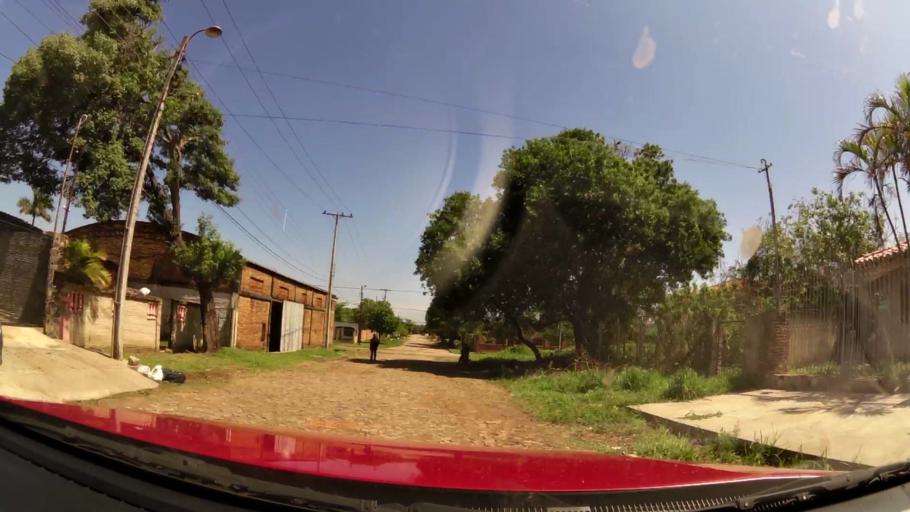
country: PY
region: Central
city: Colonia Mariano Roque Alonso
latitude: -25.2308
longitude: -57.5465
